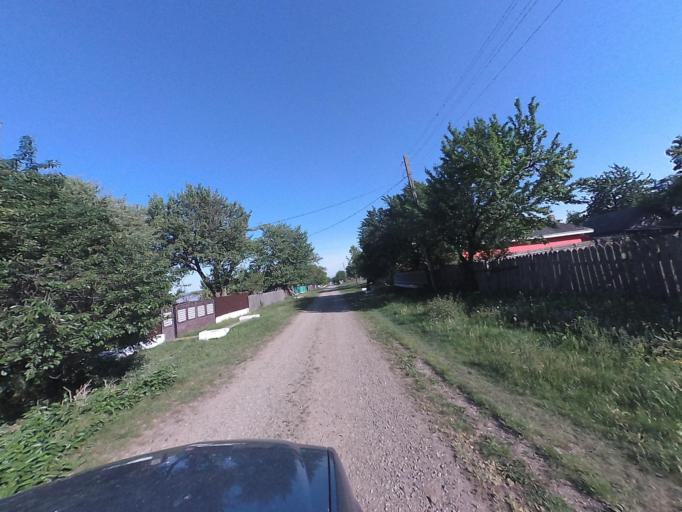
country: RO
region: Neamt
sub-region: Comuna Dulcesti
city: Dulcesti
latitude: 47.0081
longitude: 26.7665
